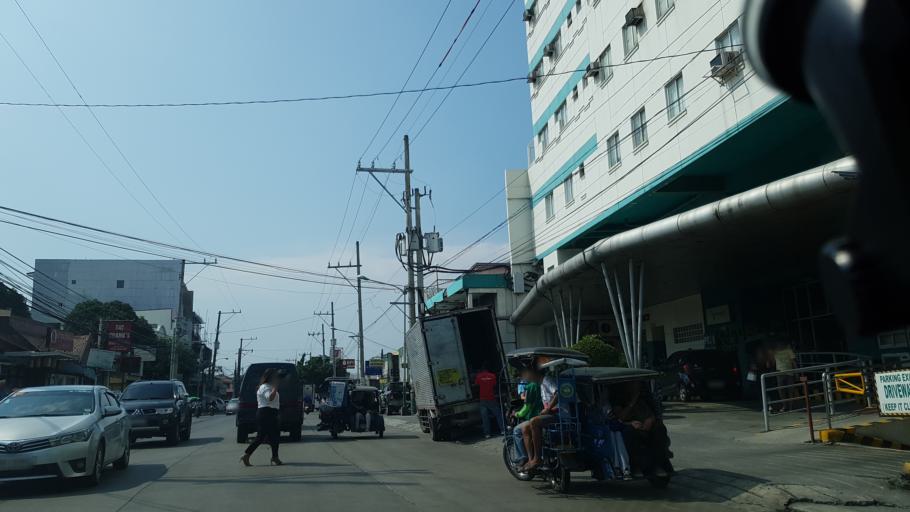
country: PH
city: Sambayanihan People's Village
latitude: 14.4856
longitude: 121.0284
